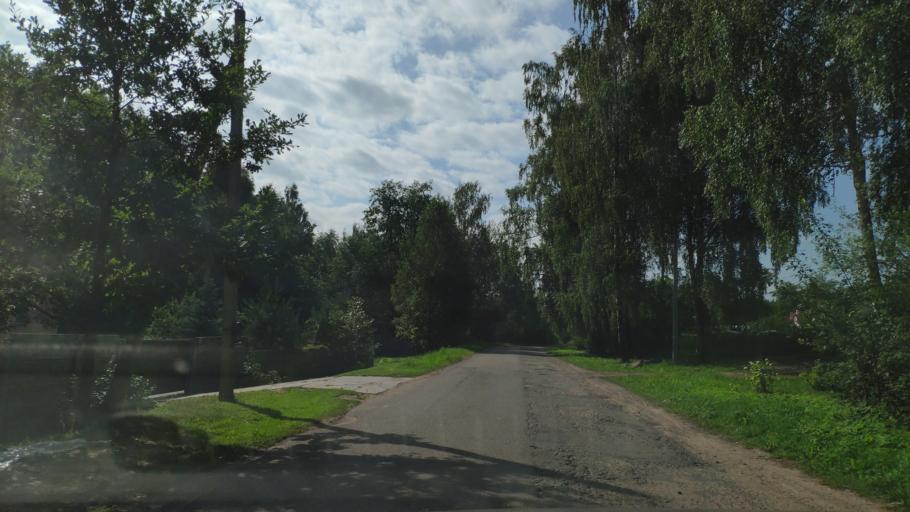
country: BY
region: Minsk
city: Zaslawye
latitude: 53.9868
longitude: 27.2885
